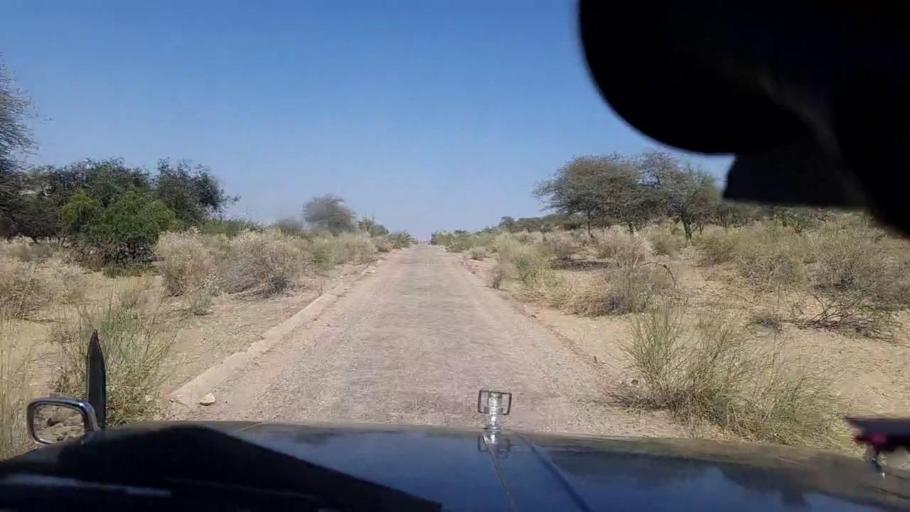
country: PK
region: Sindh
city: Diplo
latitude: 24.4161
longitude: 69.6547
